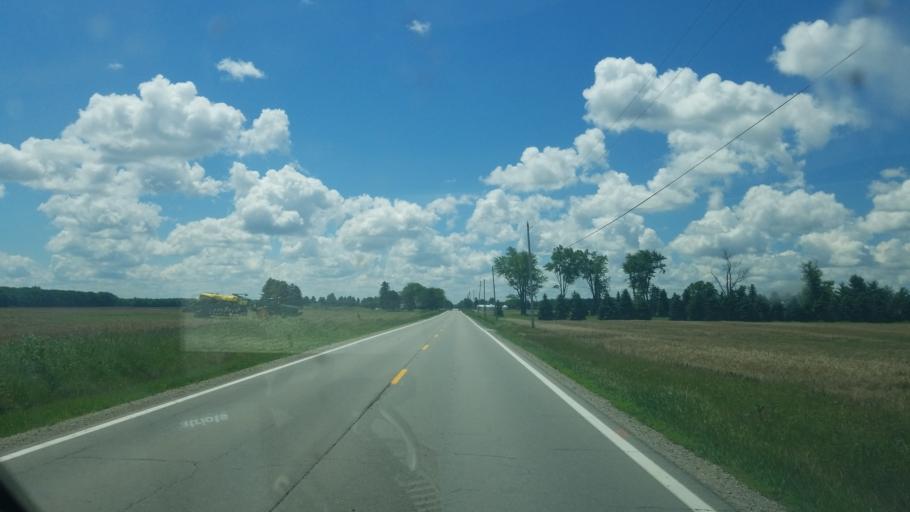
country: US
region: Ohio
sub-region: Huron County
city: New London
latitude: 41.1640
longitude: -82.4104
